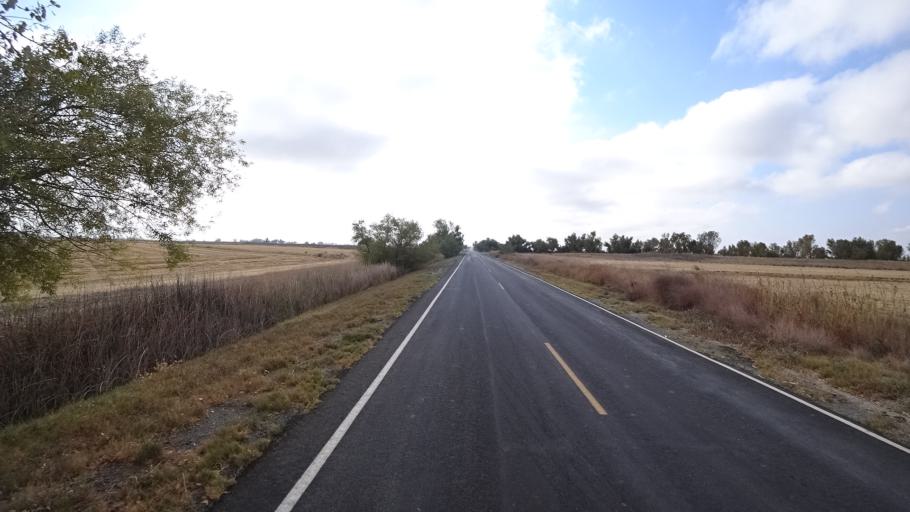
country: US
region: California
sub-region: Yolo County
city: Woodland
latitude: 38.8064
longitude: -121.7744
